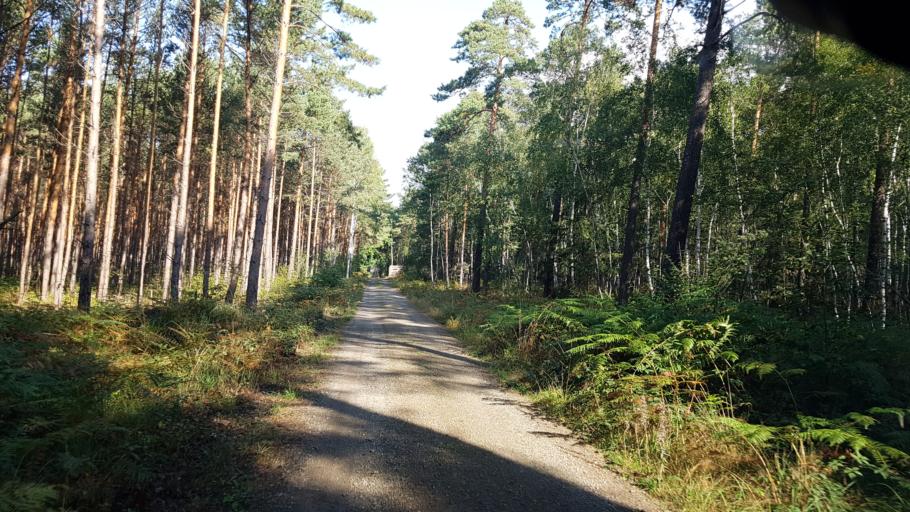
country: DE
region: Brandenburg
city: Plessa
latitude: 51.5229
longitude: 13.6390
